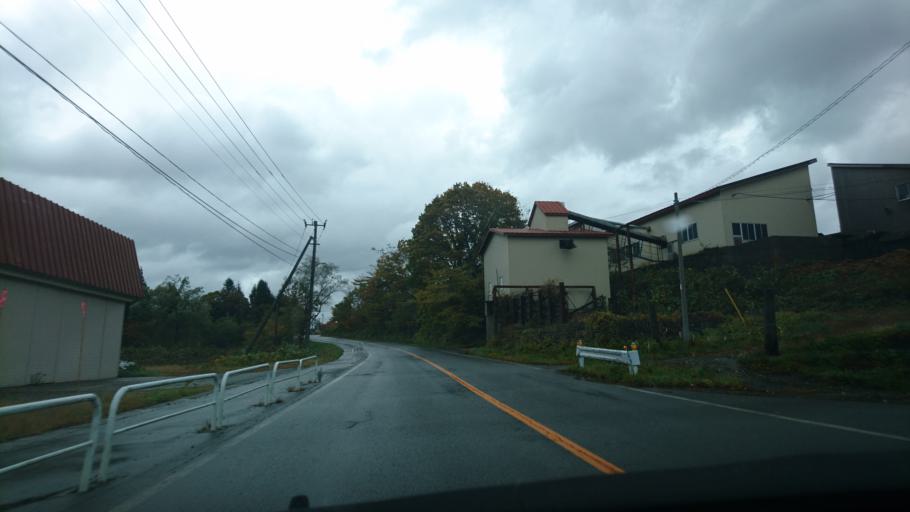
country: JP
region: Akita
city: Kakunodatemachi
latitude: 39.4506
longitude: 140.7649
